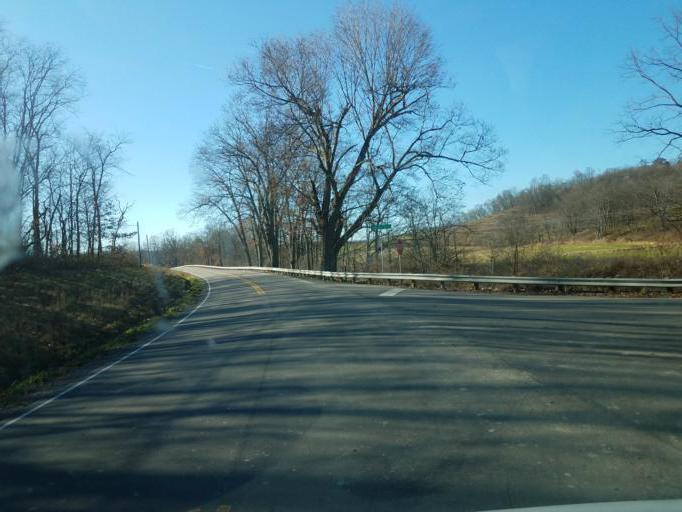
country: US
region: Ohio
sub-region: Muskingum County
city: Dresden
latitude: 40.2306
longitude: -82.0647
